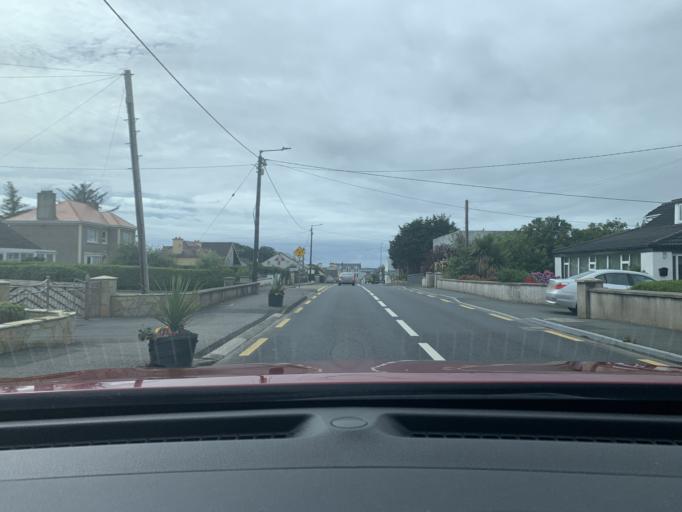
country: IE
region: Ulster
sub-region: County Donegal
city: Dungloe
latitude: 54.9504
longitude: -8.3563
